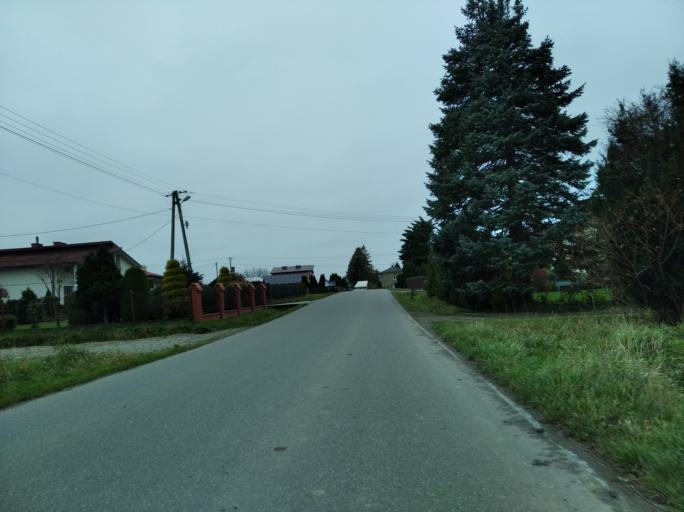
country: PL
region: Subcarpathian Voivodeship
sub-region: Powiat krosnienski
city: Jedlicze
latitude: 49.6857
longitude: 21.6701
